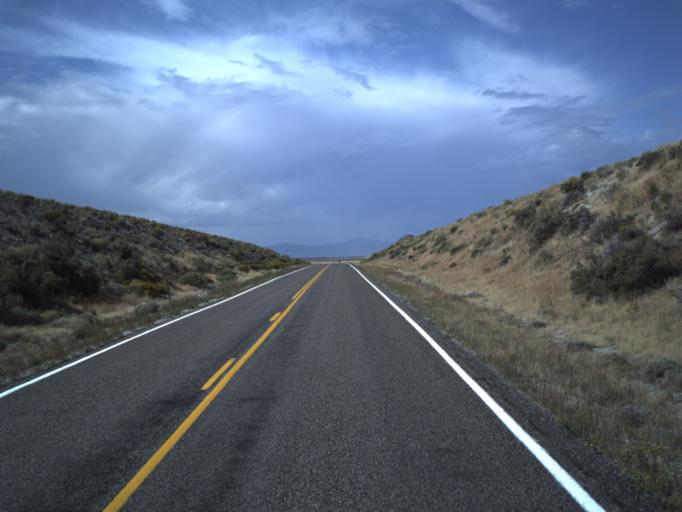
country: US
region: Utah
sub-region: Tooele County
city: Wendover
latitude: 41.4047
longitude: -113.9419
